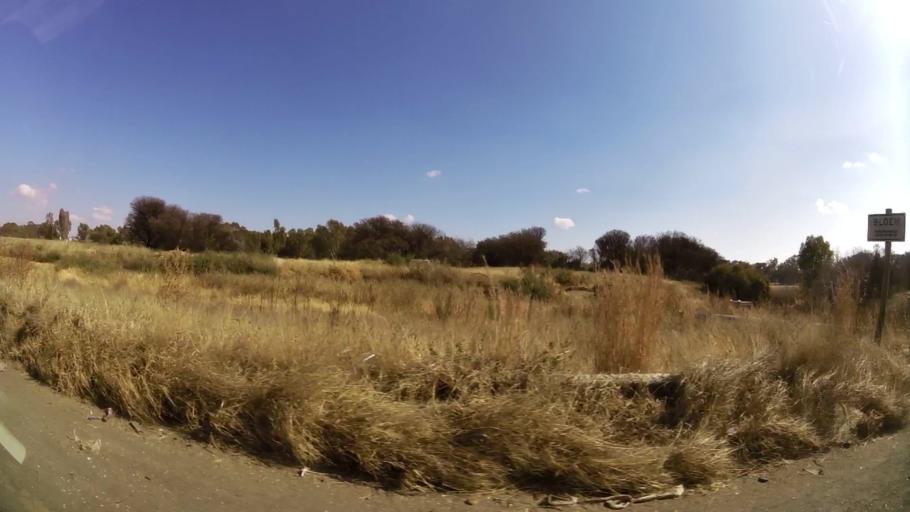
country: ZA
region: Orange Free State
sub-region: Mangaung Metropolitan Municipality
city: Bloemfontein
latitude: -29.1217
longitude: 26.2671
